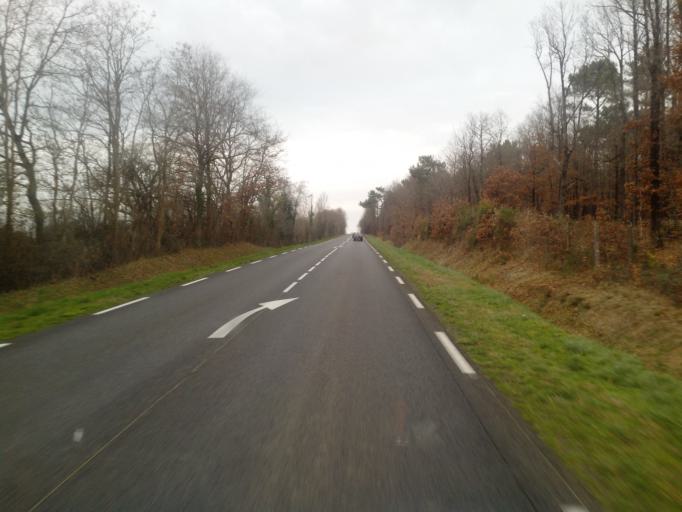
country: FR
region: Poitou-Charentes
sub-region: Departement de la Vienne
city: Lussac-les-Chateaux
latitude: 46.3518
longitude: 0.7865
